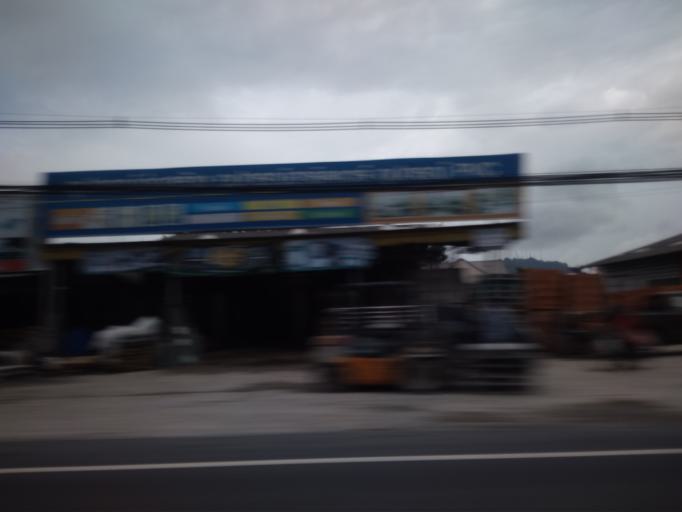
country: TH
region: Phuket
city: Ban Ko Kaeo
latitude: 7.9197
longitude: 98.3700
